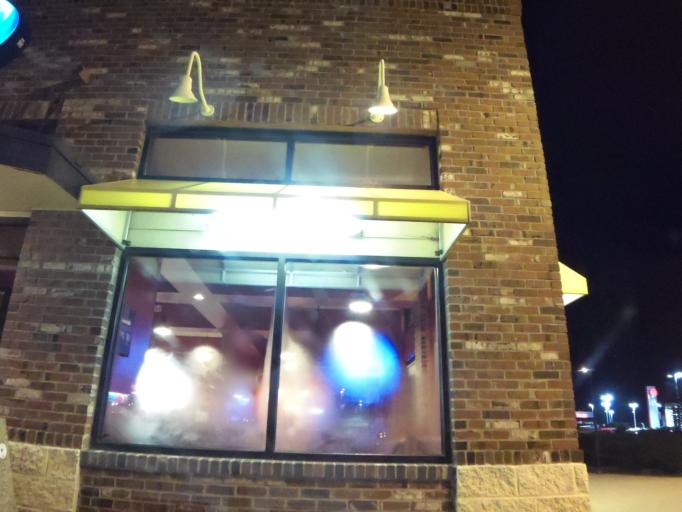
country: US
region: Indiana
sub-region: Marion County
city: Southport
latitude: 39.6450
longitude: -86.1329
